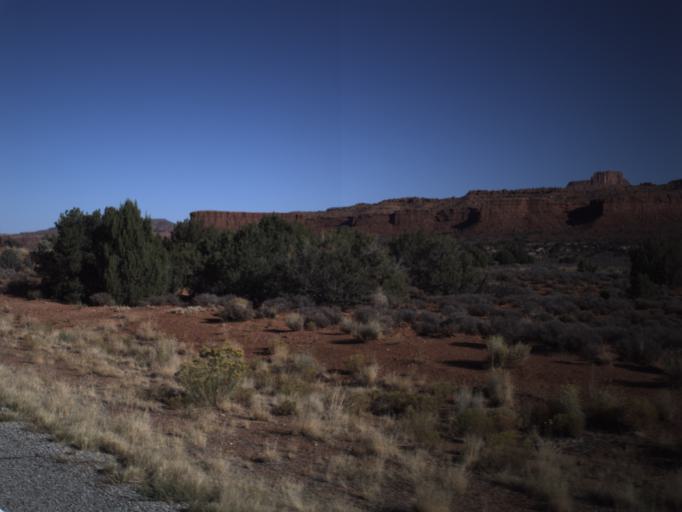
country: US
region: Utah
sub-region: San Juan County
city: Blanding
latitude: 37.6714
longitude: -110.2025
